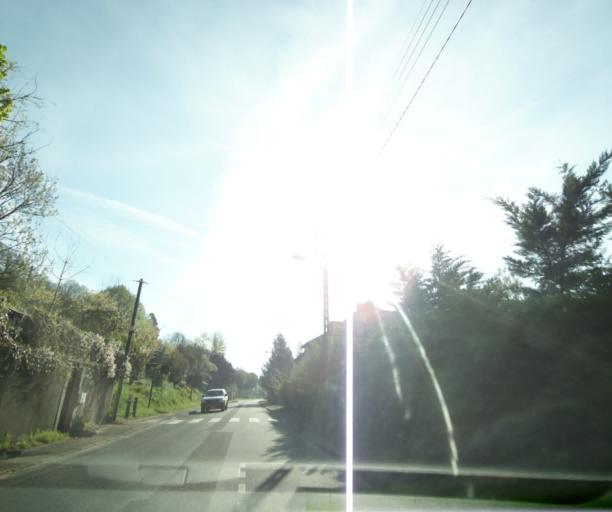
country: FR
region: Ile-de-France
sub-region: Departement de Seine-et-Marne
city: Saint-Mammes
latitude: 48.3937
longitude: 2.8201
